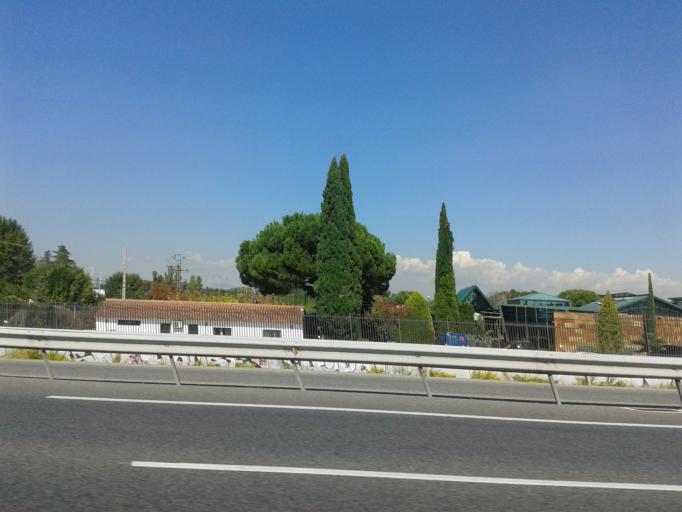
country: ES
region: Madrid
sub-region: Provincia de Madrid
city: San Fernando de Henares
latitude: 40.4485
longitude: -3.5260
